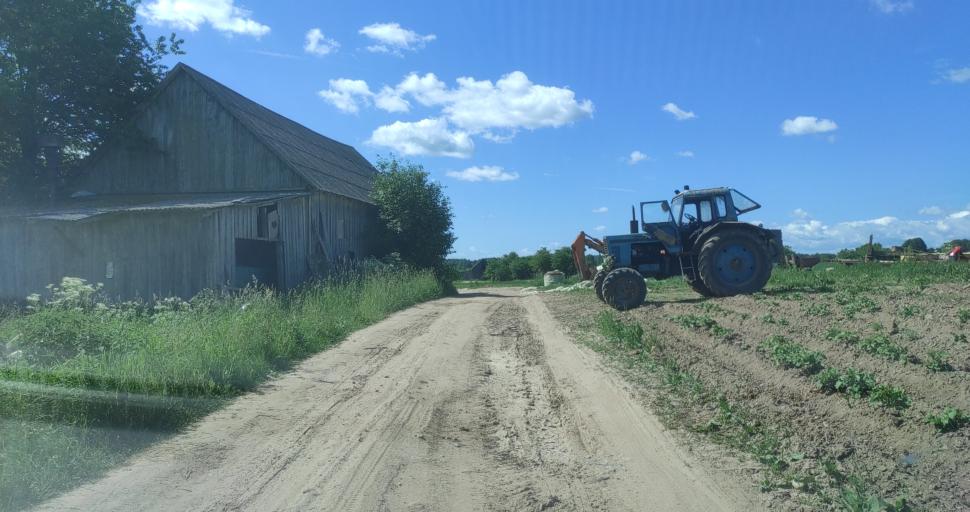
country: LV
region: Alsunga
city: Alsunga
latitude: 56.9059
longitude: 21.7230
